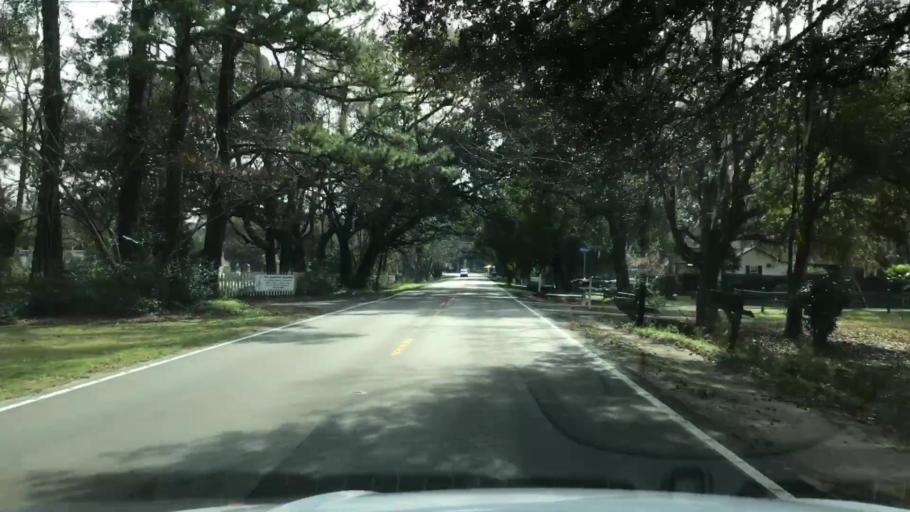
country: US
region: South Carolina
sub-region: Charleston County
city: Shell Point
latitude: 32.7348
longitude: -80.0317
